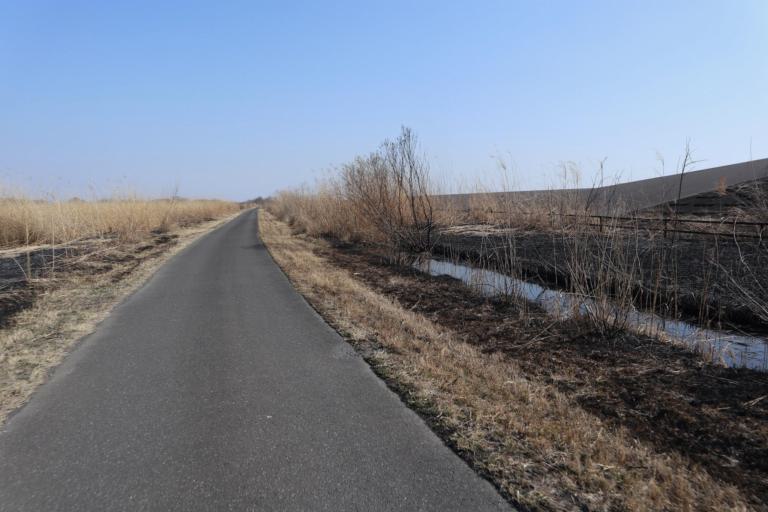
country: JP
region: Tochigi
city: Fujioka
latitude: 36.2550
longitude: 139.6647
